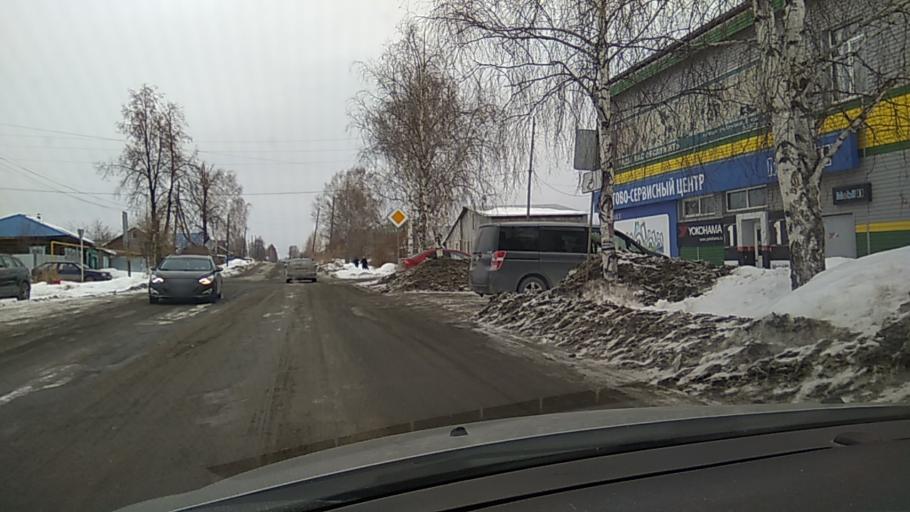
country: RU
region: Sverdlovsk
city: Revda
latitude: 56.8062
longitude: 59.9356
